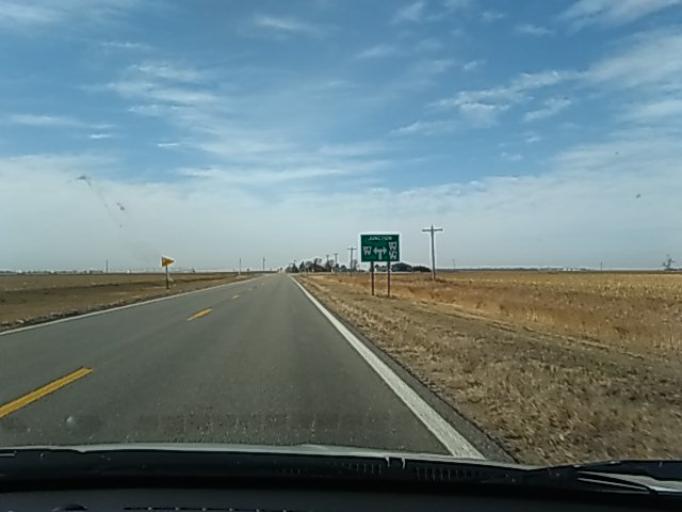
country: US
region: Nebraska
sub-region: Clay County
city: Clay Center
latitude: 40.4233
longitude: -98.0473
